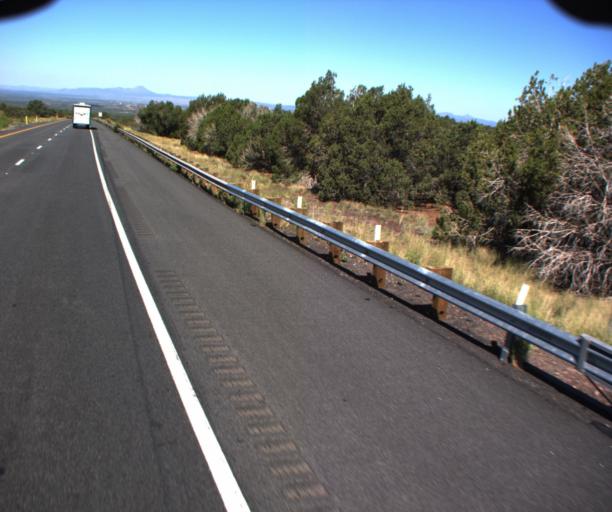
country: US
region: Arizona
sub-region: Coconino County
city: Williams
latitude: 35.2162
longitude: -112.3820
